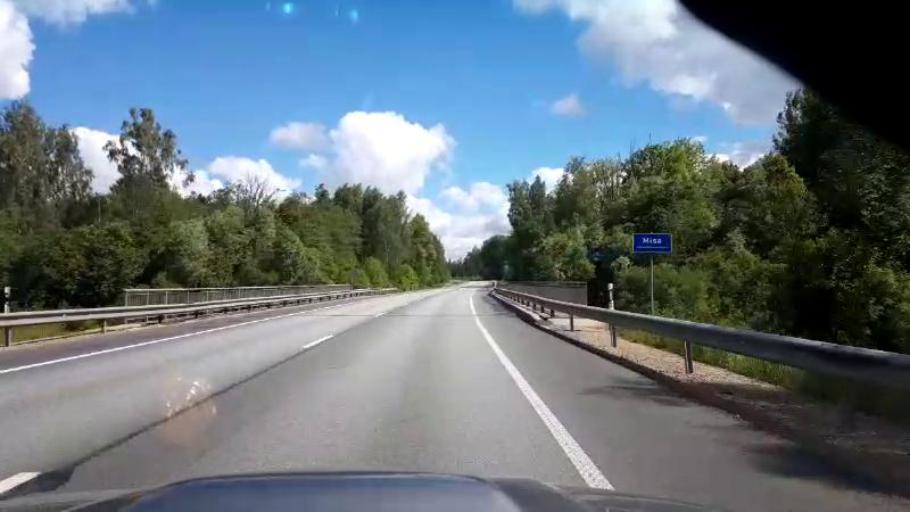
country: LV
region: Kekava
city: Kekava
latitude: 56.7189
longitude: 24.2510
